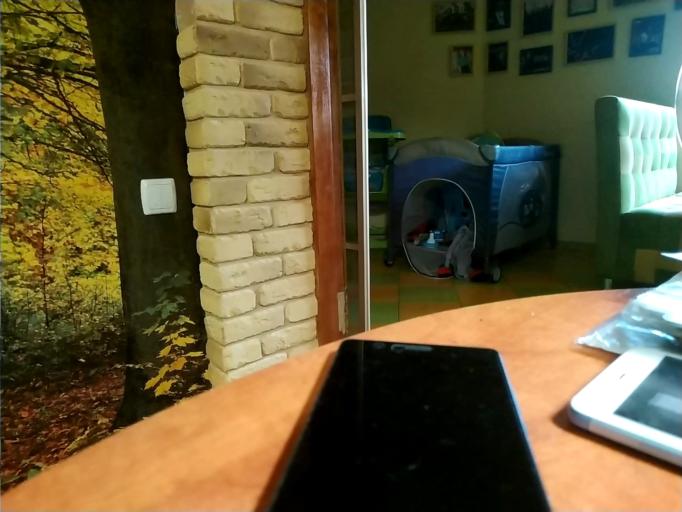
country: RU
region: Kaluga
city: Khvastovichi
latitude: 53.6378
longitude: 35.4550
